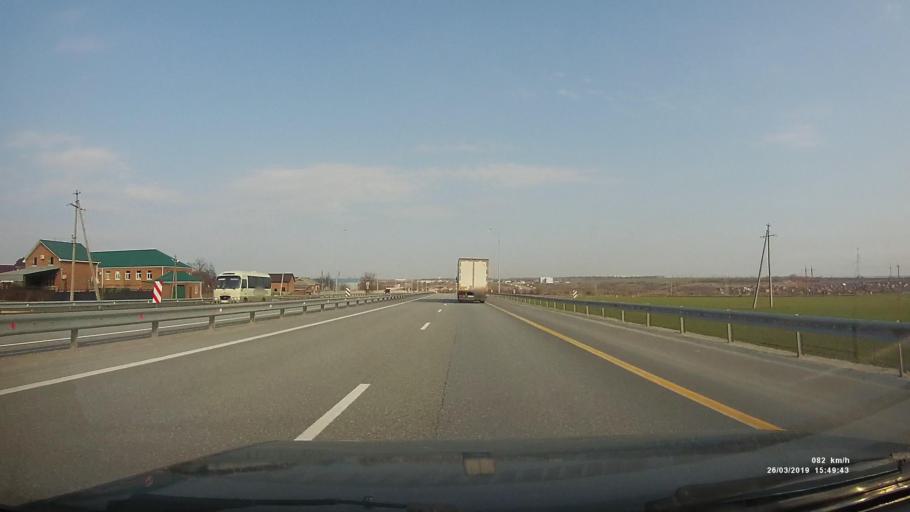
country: RU
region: Rostov
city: Chaltyr
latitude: 47.2753
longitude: 39.4737
